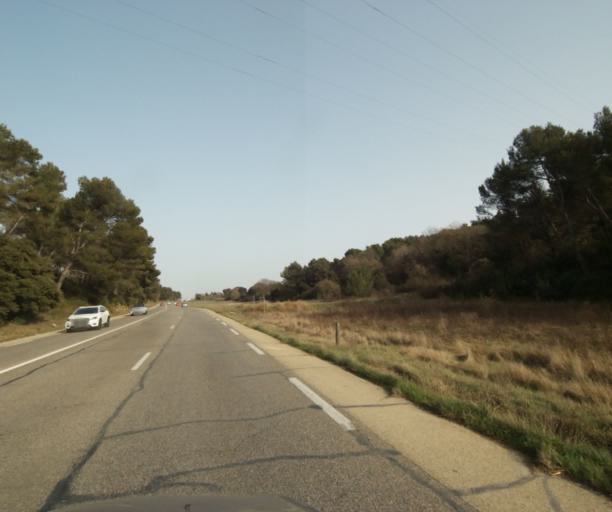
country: FR
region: Provence-Alpes-Cote d'Azur
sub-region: Departement des Bouches-du-Rhone
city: Les Pennes-Mirabeau
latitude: 43.4132
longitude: 5.3407
